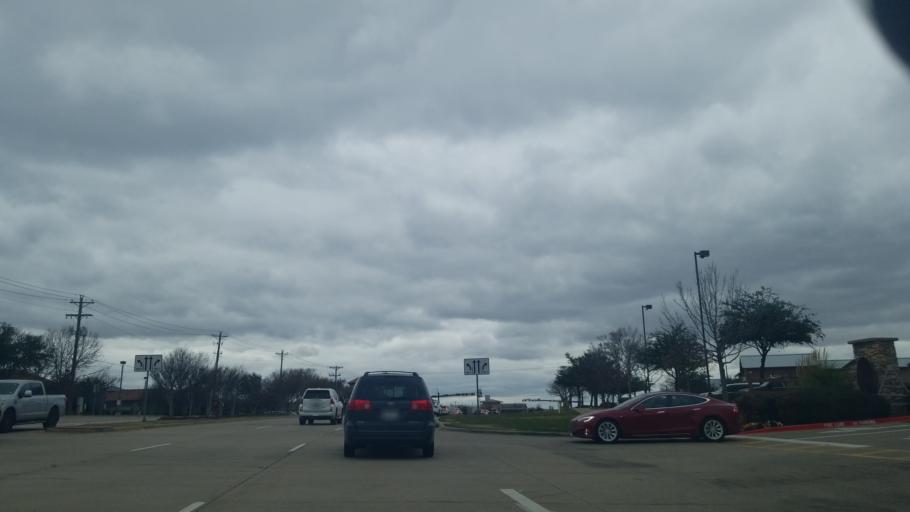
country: US
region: Texas
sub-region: Denton County
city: Double Oak
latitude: 33.0701
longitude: -97.0829
